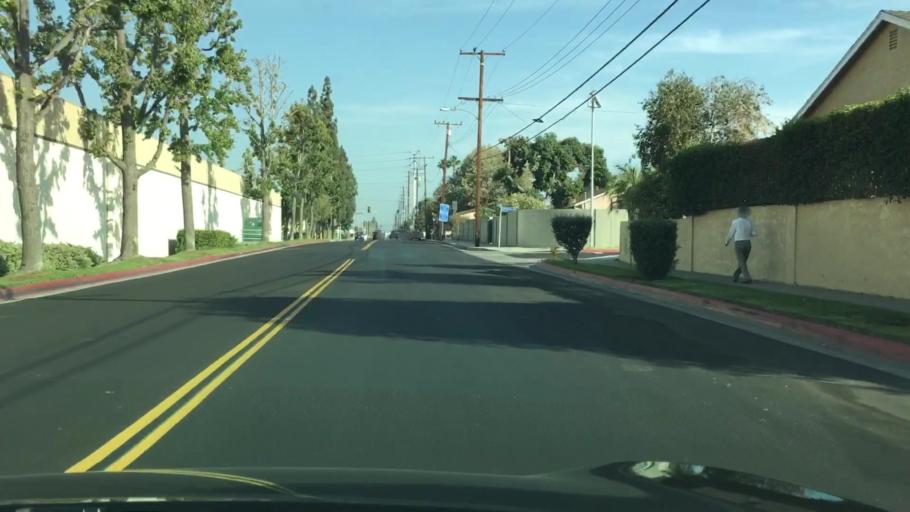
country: US
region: California
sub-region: Los Angeles County
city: Avocado Heights
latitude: 34.0241
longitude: -117.9879
